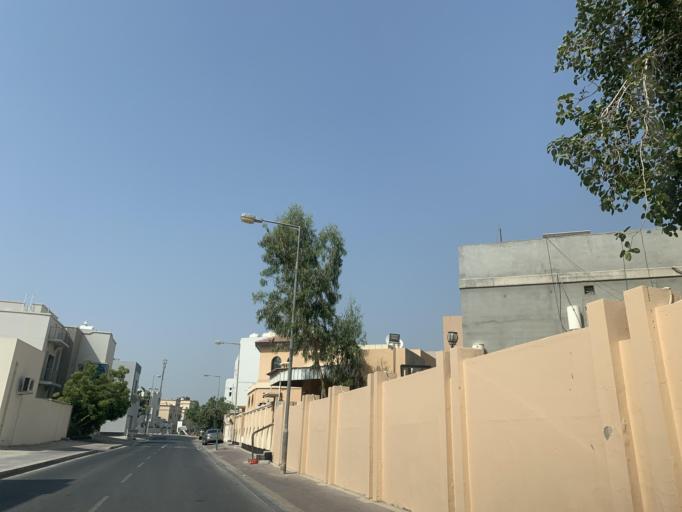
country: BH
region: Manama
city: Jidd Hafs
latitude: 26.2070
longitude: 50.5312
